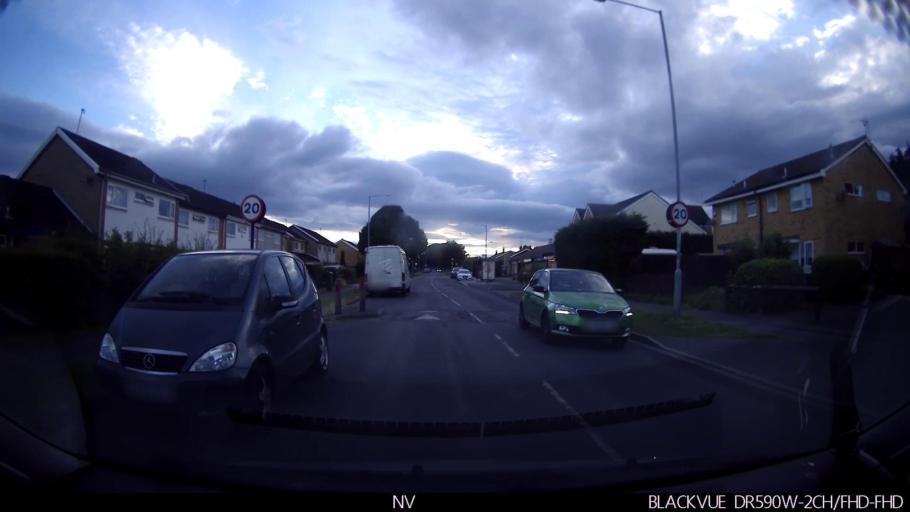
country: GB
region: England
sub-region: City of York
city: Copmanthorpe
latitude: 53.9429
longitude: -1.1319
